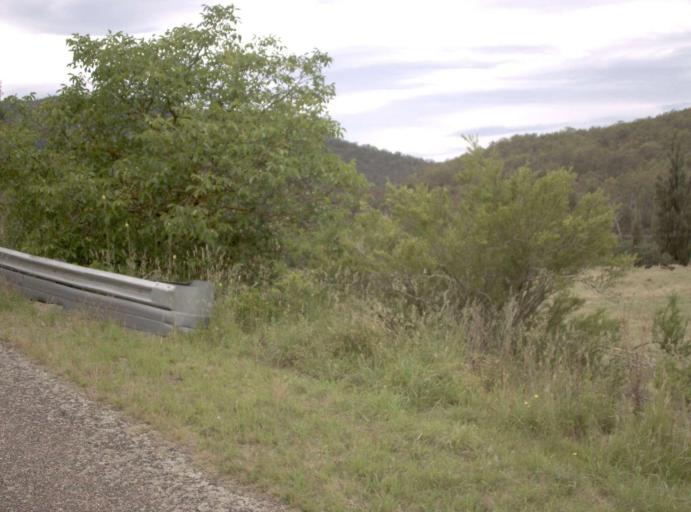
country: AU
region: Victoria
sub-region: East Gippsland
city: Bairnsdale
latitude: -37.5143
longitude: 147.2022
